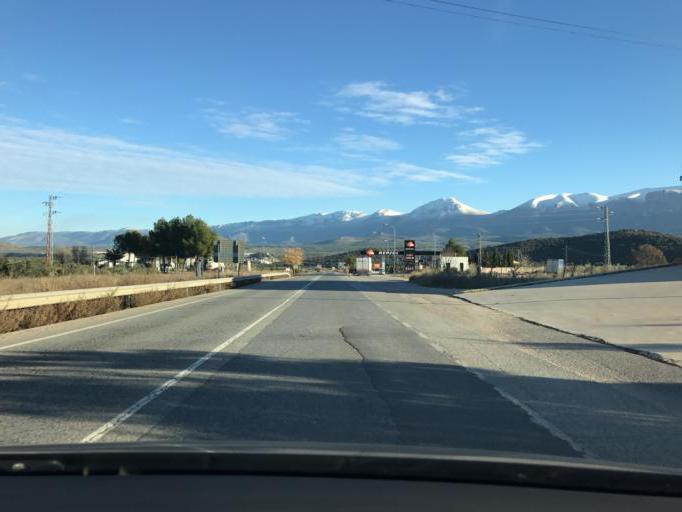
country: ES
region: Andalusia
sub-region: Provincia de Granada
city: Iznalloz
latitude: 37.4016
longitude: -3.5561
